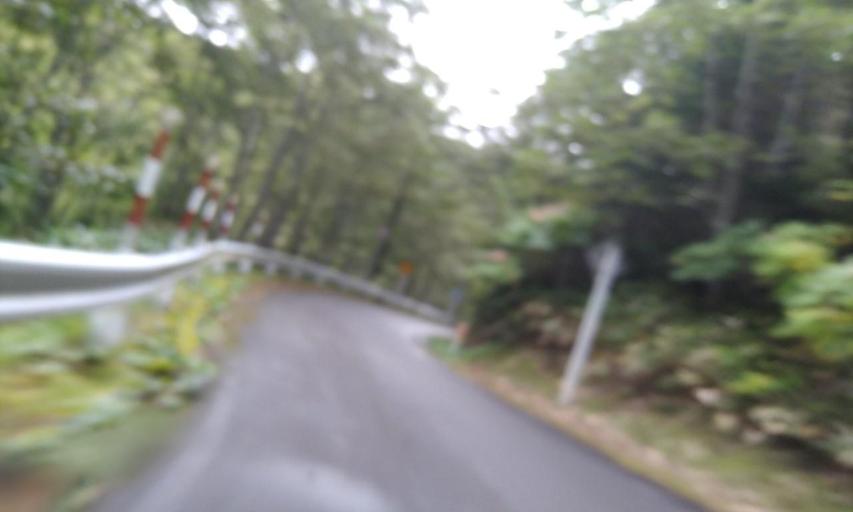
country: JP
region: Hokkaido
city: Bihoro
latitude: 43.5708
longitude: 144.2000
